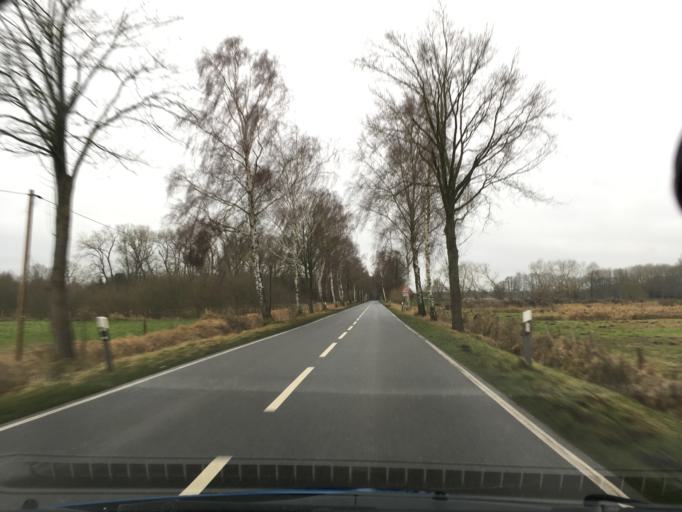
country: DE
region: Lower Saxony
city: Bleckede
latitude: 53.3133
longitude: 10.6710
